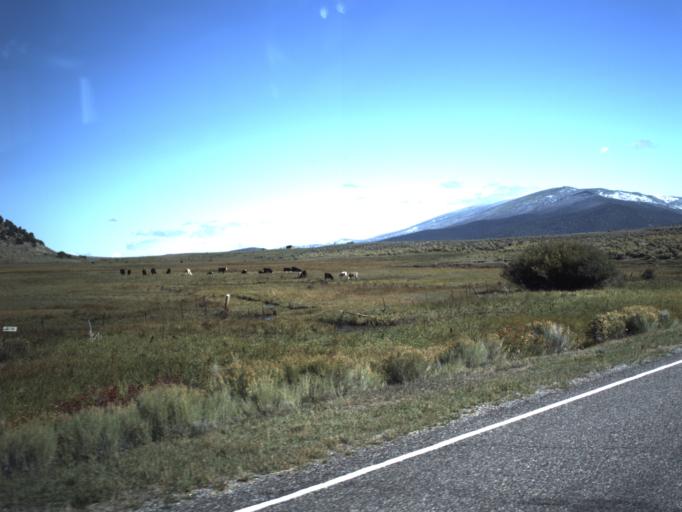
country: US
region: Utah
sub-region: Wayne County
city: Loa
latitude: 38.5640
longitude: -111.8490
